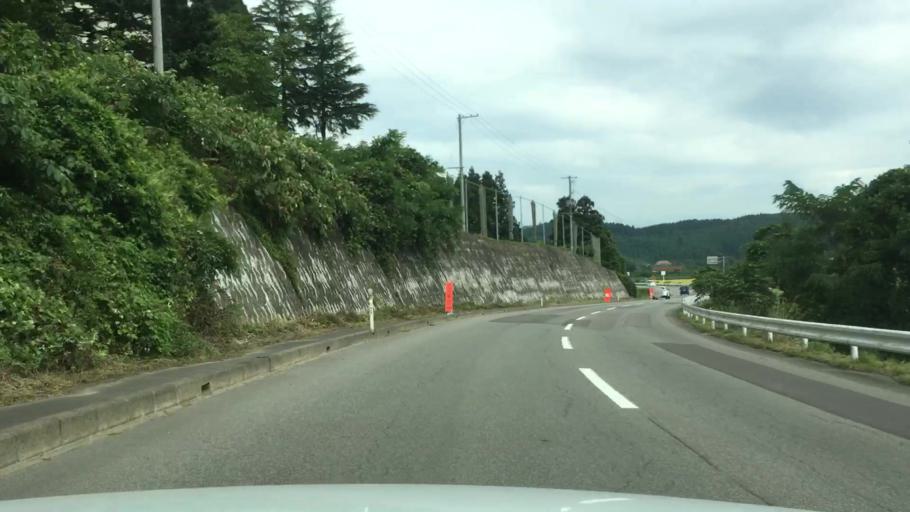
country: JP
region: Aomori
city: Shimokizukuri
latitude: 40.7517
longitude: 140.2294
